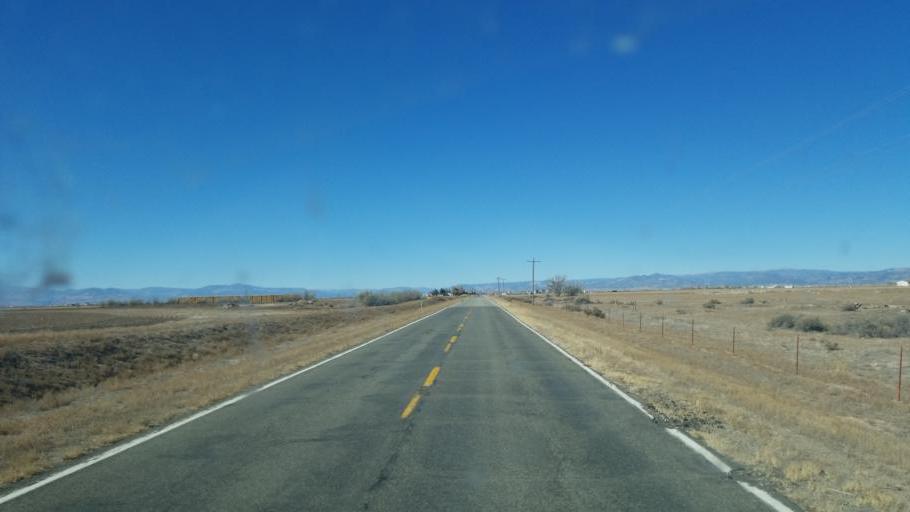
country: US
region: Colorado
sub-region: Saguache County
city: Center
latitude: 37.7485
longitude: -106.0064
